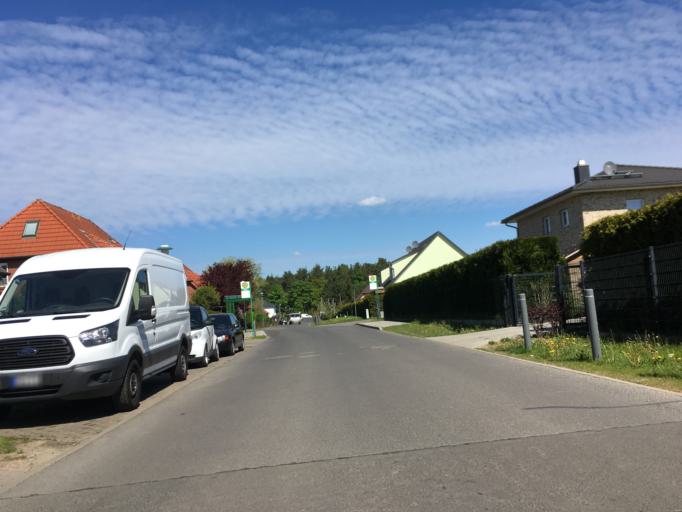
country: DE
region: Berlin
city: Buch
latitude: 52.6779
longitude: 13.5268
